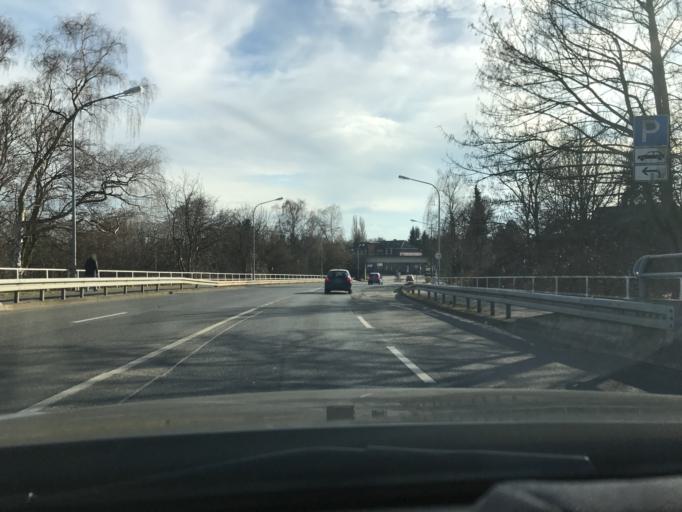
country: DE
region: North Rhine-Westphalia
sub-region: Regierungsbezirk Dusseldorf
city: Krefeld
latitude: 51.3298
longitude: 6.6141
